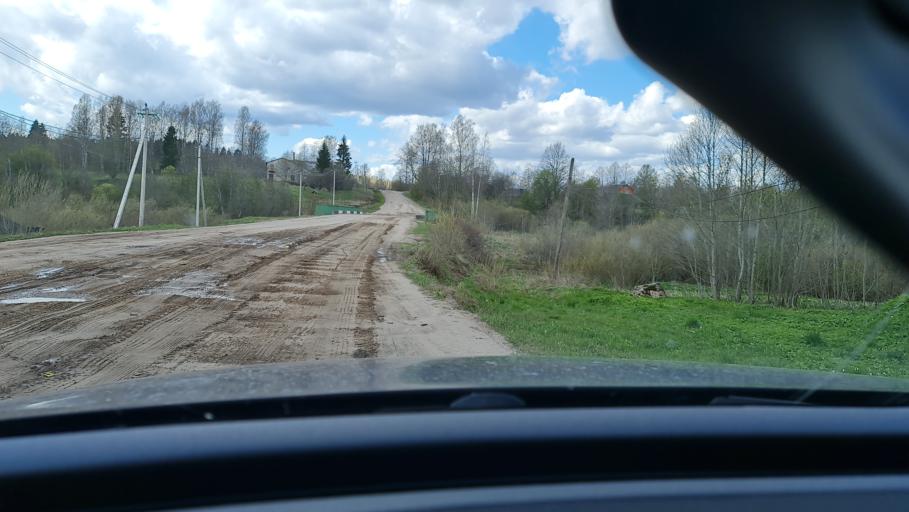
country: RU
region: Tverskaya
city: Toropets
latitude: 56.6443
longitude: 31.4261
